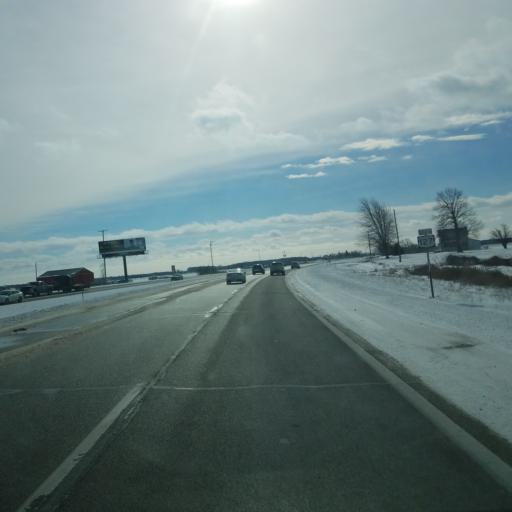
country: US
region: Michigan
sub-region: Gratiot County
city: Ithaca
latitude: 43.2677
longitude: -84.5638
